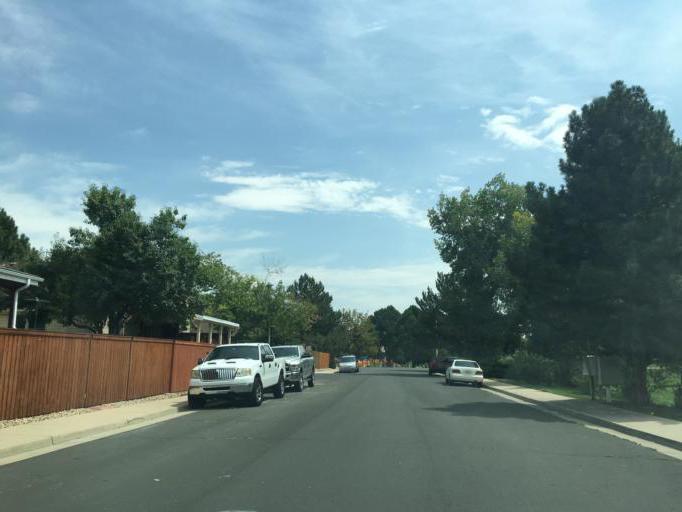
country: US
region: Colorado
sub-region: Adams County
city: Aurora
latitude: 39.7282
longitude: -104.8017
